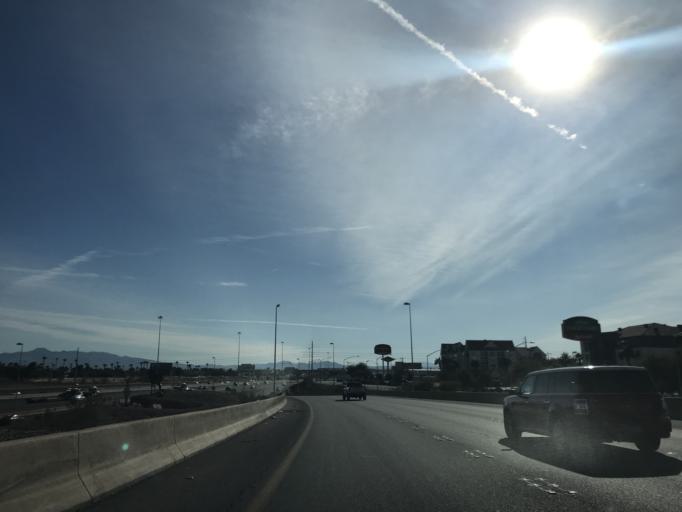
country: US
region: Nevada
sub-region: Clark County
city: Paradise
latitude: 36.0853
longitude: -115.1821
